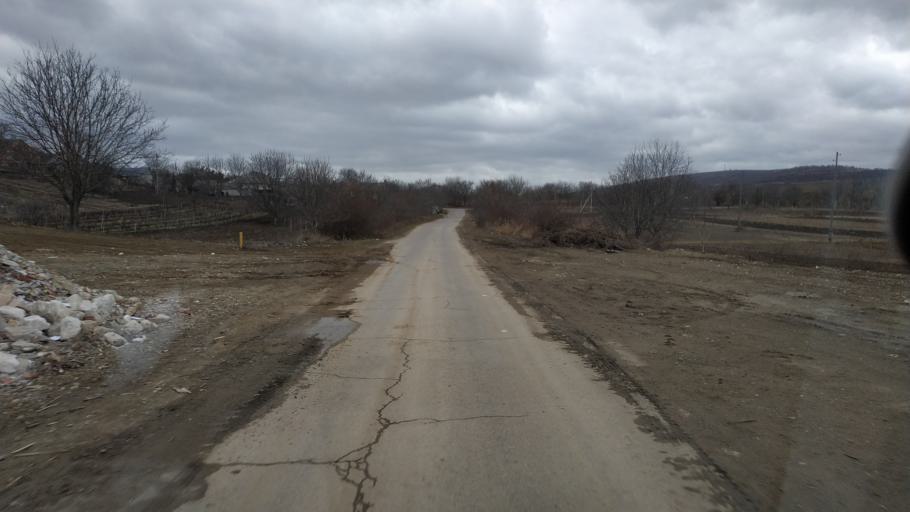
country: MD
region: Calarasi
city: Calarasi
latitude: 47.2453
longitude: 28.2893
